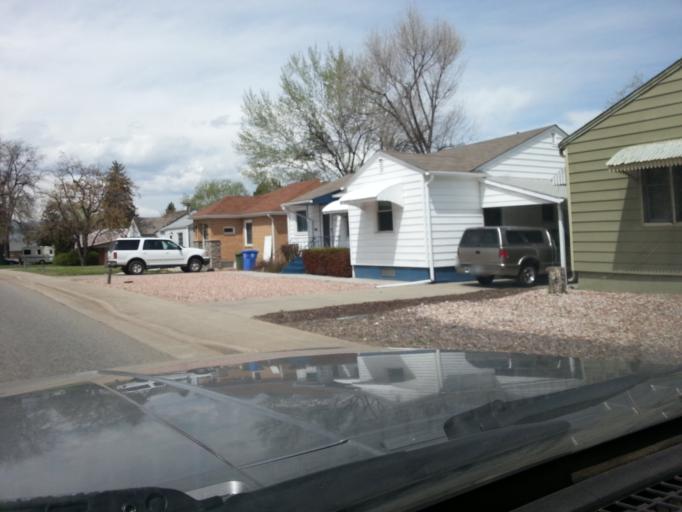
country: US
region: Colorado
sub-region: Larimer County
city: Loveland
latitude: 40.4073
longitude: -105.0789
